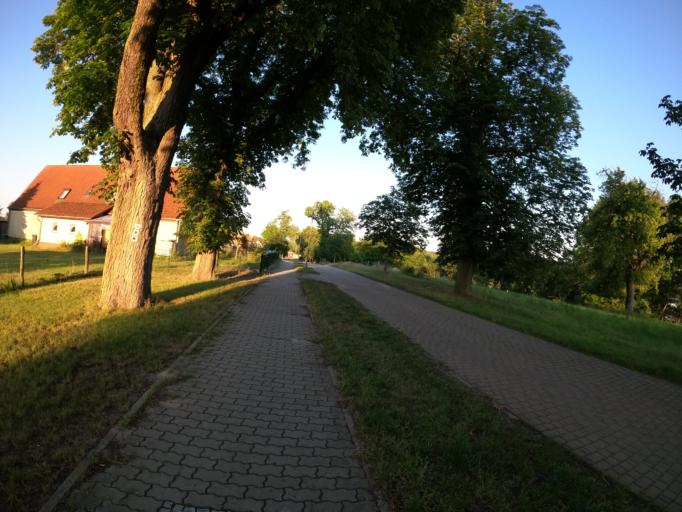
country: DE
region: Brandenburg
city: Angermunde
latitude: 53.0253
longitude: 13.8945
